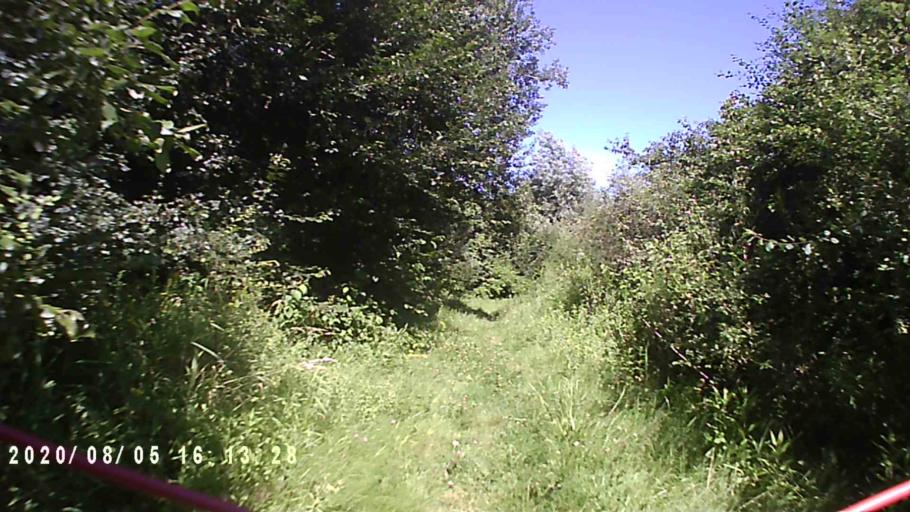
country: NL
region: Groningen
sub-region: Gemeente Winsum
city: Winsum
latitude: 53.3981
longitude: 6.5245
